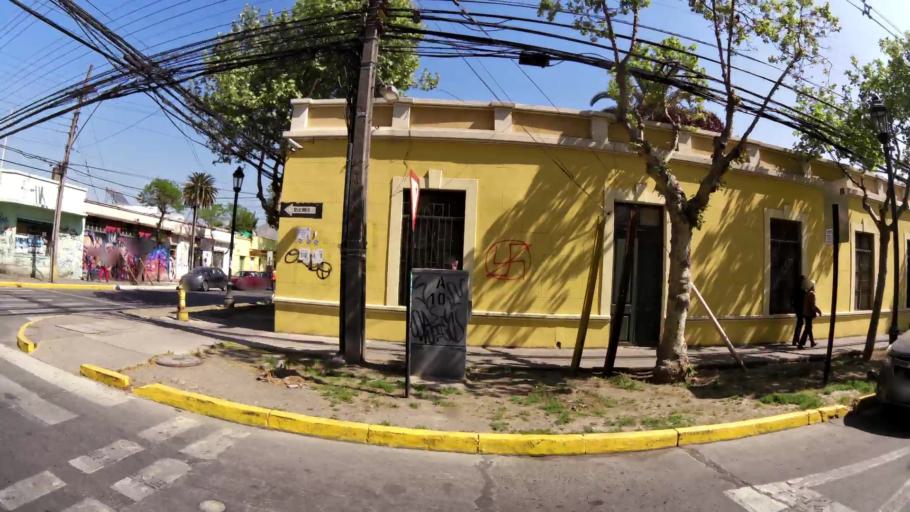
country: CL
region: Santiago Metropolitan
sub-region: Provincia de Maipo
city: San Bernardo
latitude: -33.5935
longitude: -70.7013
